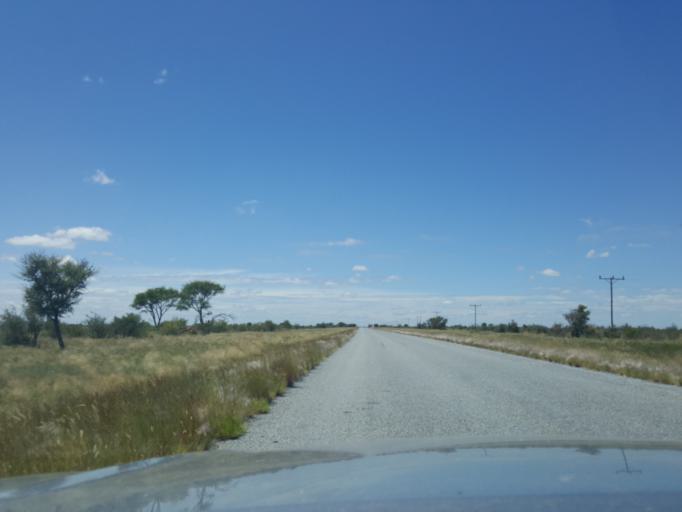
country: BW
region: Central
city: Nata
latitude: -20.1962
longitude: 26.0983
